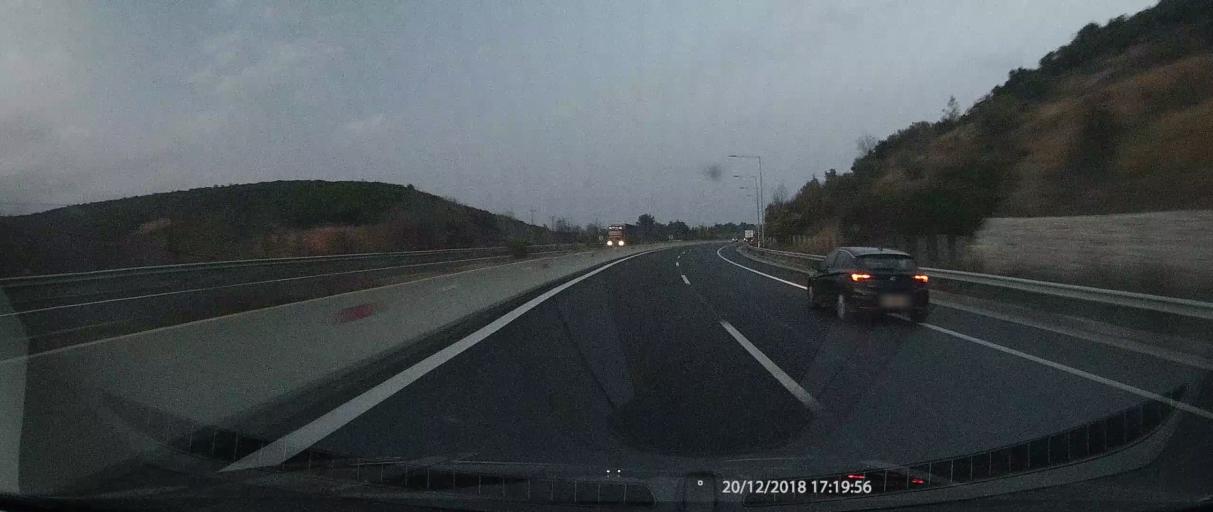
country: GR
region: Thessaly
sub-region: Nomos Larisis
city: Pyrgetos
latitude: 39.9549
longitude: 22.6456
